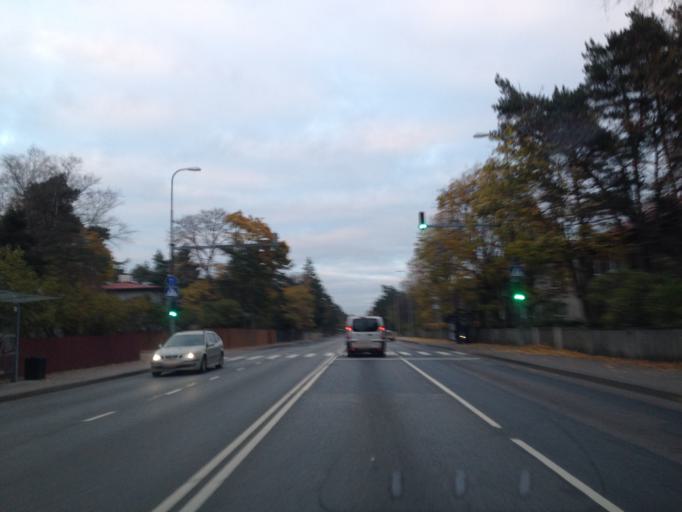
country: EE
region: Harju
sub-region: Saue vald
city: Laagri
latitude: 59.3699
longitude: 24.6570
